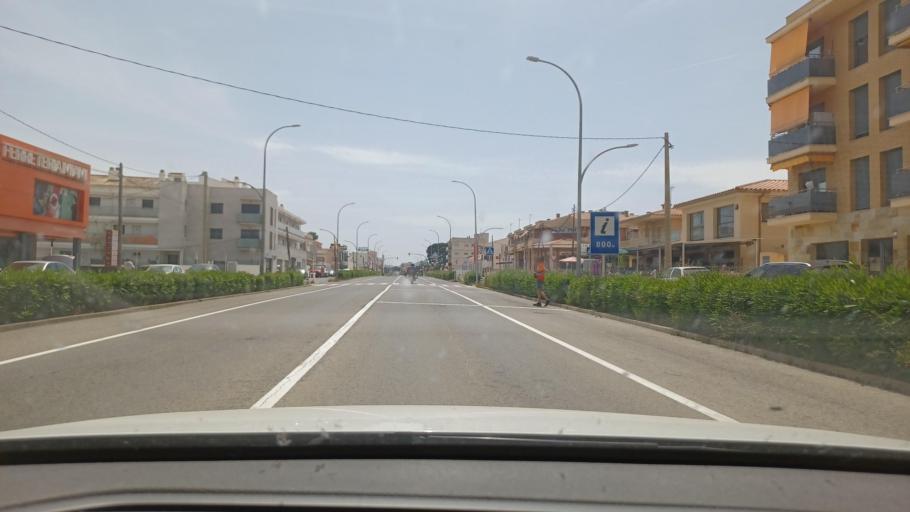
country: ES
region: Catalonia
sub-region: Provincia de Tarragona
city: Vilanova d'Escornalbou
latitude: 41.0140
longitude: 0.9454
